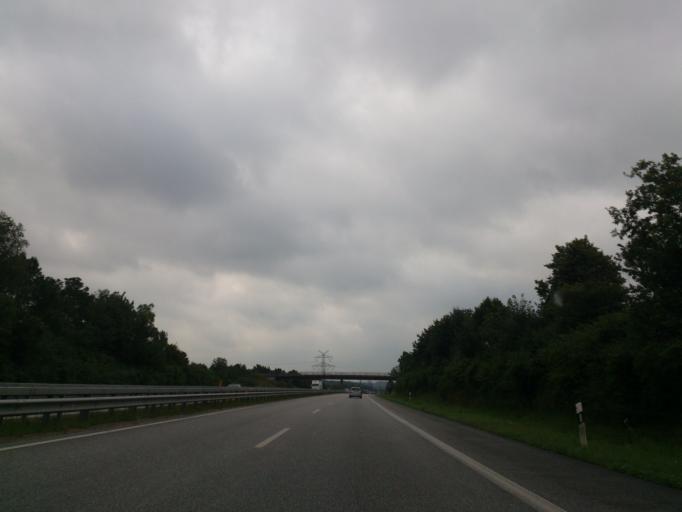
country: DE
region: Schleswig-Holstein
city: Kaisborstel
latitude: 54.0072
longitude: 9.4771
